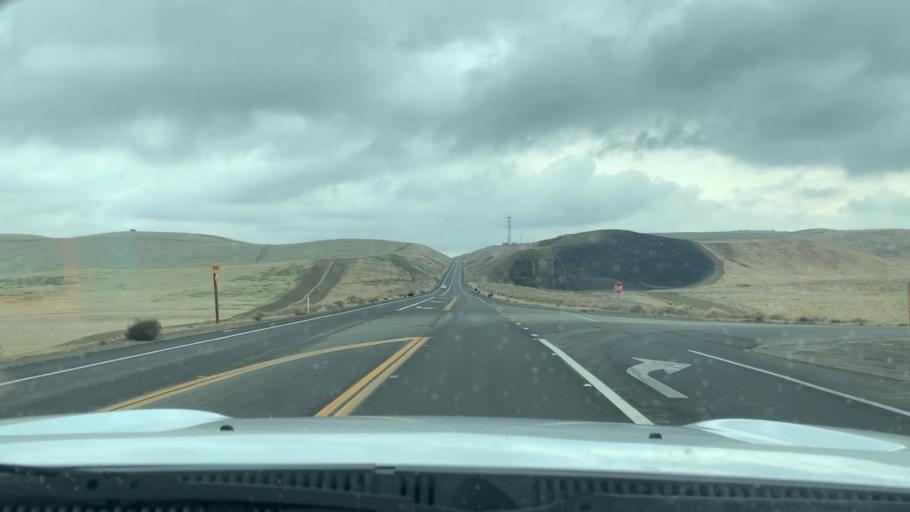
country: US
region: California
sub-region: Kings County
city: Kettleman City
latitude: 35.9542
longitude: -119.9931
